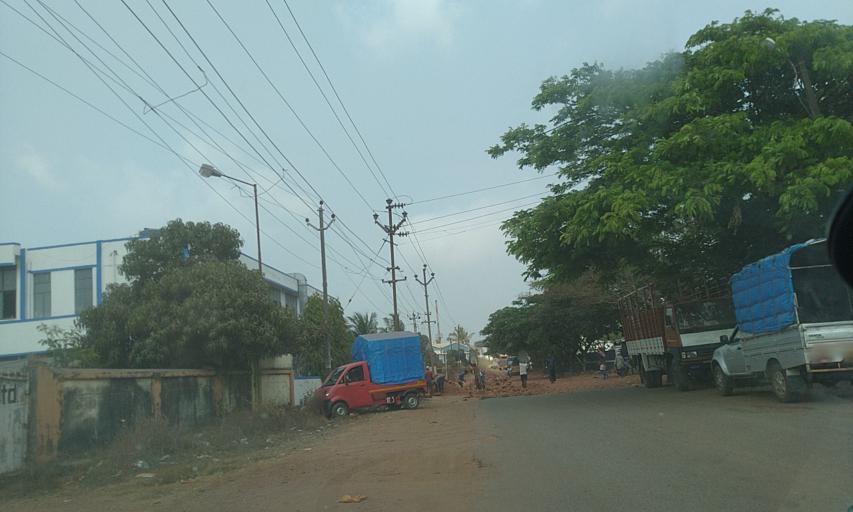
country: IN
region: Goa
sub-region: South Goa
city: Sancoale
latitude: 15.3751
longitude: 73.9299
